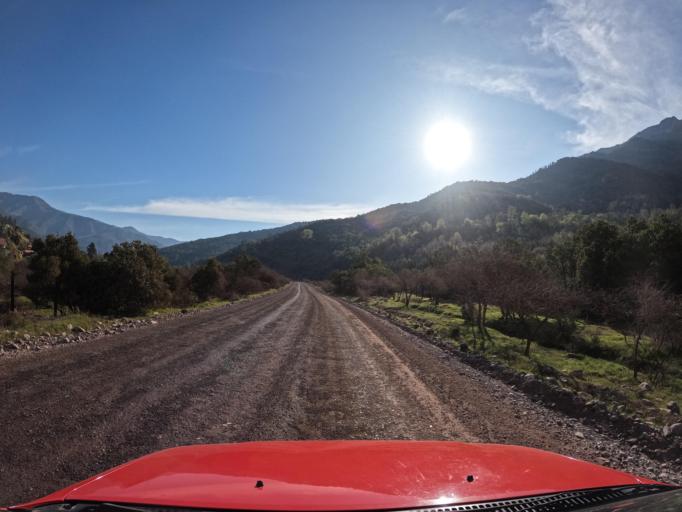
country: CL
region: O'Higgins
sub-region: Provincia de Colchagua
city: Chimbarongo
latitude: -34.9955
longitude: -70.8169
